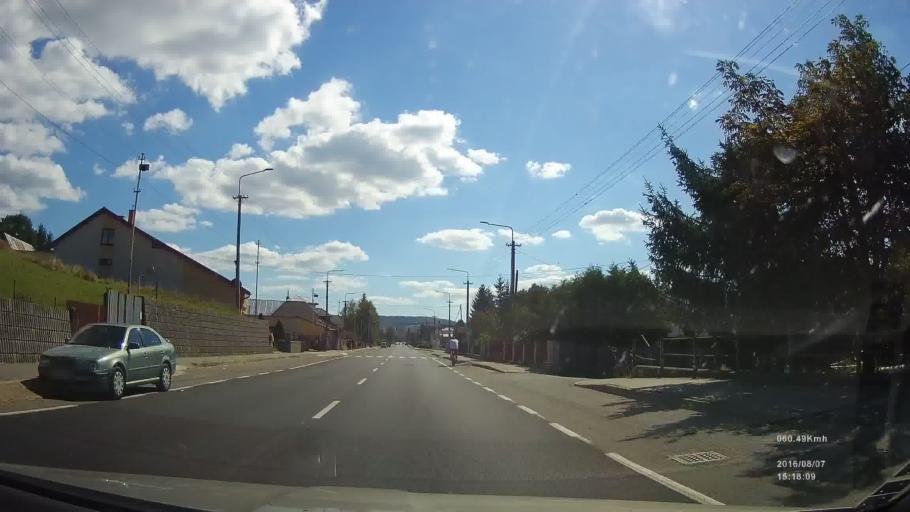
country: SK
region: Presovsky
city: Stropkov
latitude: 49.2132
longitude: 21.6564
